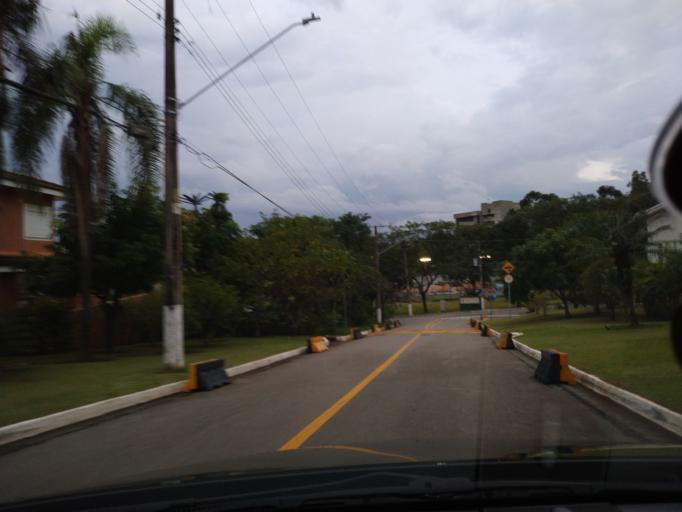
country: BR
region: Sao Paulo
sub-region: Santana De Parnaiba
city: Santana de Parnaiba
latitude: -23.4510
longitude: -46.8884
